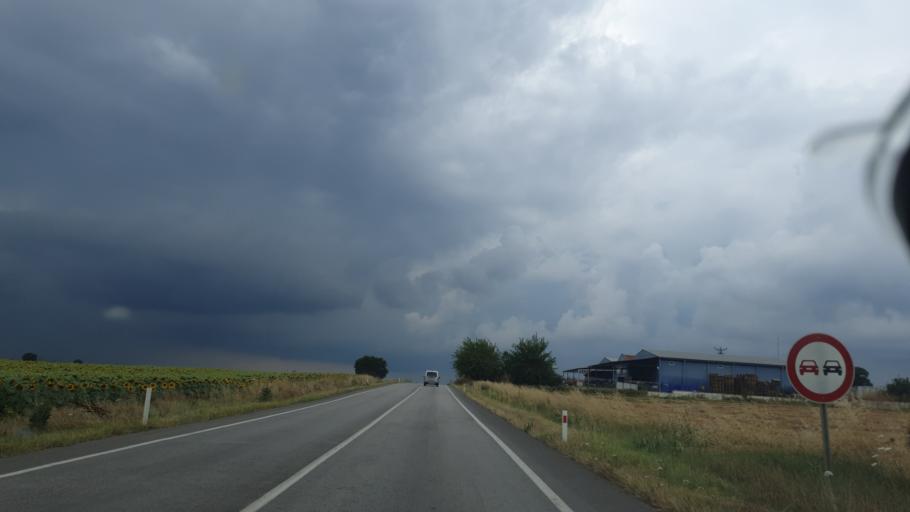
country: TR
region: Tekirdag
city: Hayrabolu
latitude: 41.2187
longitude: 27.0807
